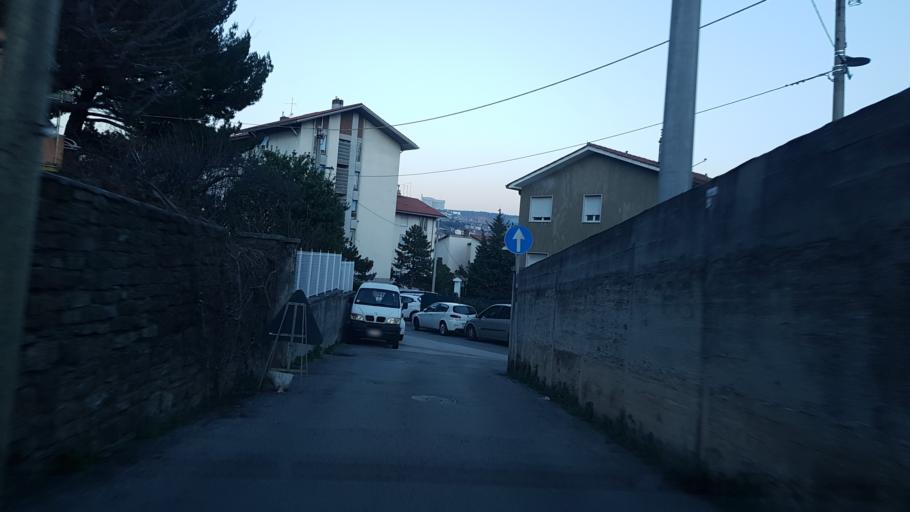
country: IT
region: Friuli Venezia Giulia
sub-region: Provincia di Trieste
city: Trieste
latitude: 45.6262
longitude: 13.7903
